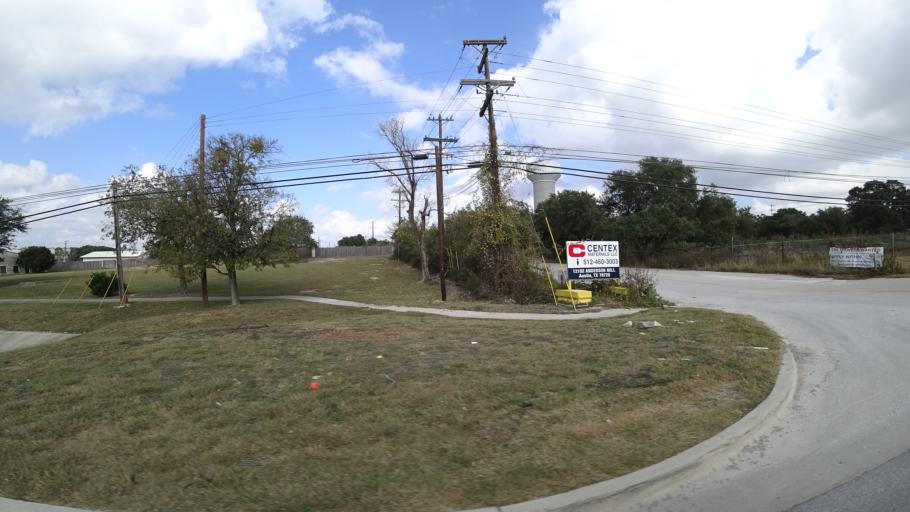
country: US
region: Texas
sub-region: Williamson County
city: Anderson Mill
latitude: 30.4567
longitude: -97.8306
